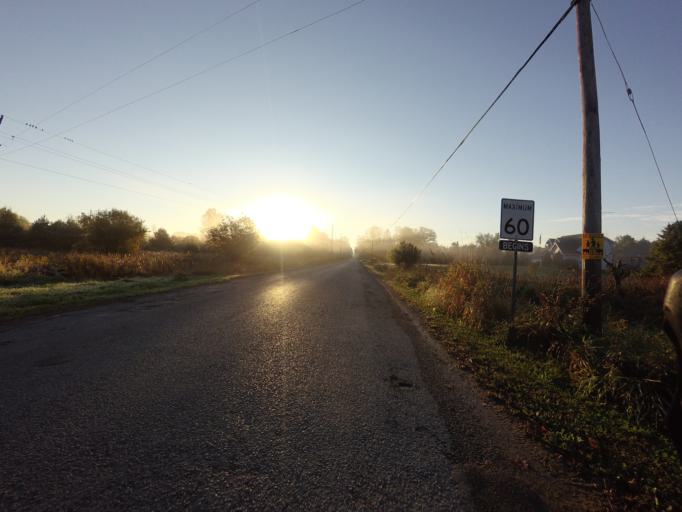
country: CA
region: Ontario
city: Quinte West
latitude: 44.0380
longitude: -77.5911
